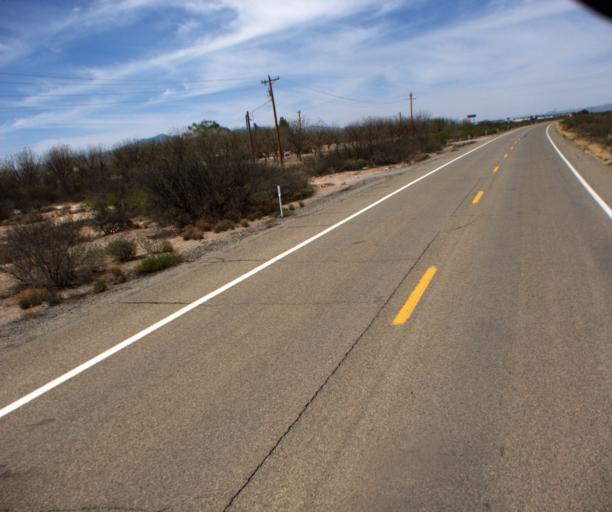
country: US
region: New Mexico
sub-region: Hidalgo County
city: Lordsburg
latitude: 32.2685
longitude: -109.2352
